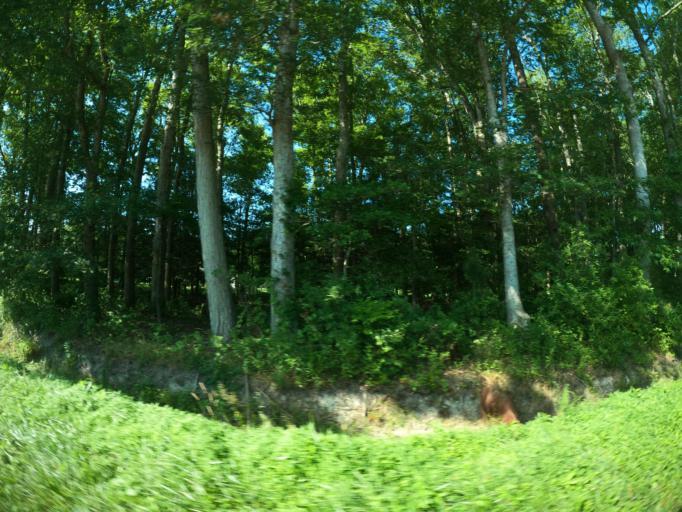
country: US
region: Delaware
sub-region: Sussex County
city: Ocean View
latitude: 38.4887
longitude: -75.1187
